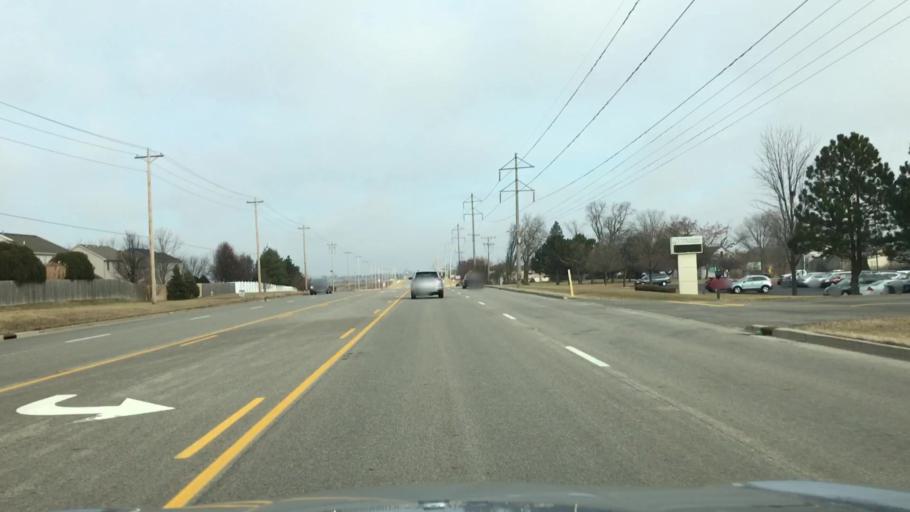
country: US
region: Illinois
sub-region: McLean County
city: Normal
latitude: 40.5100
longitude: -88.9027
